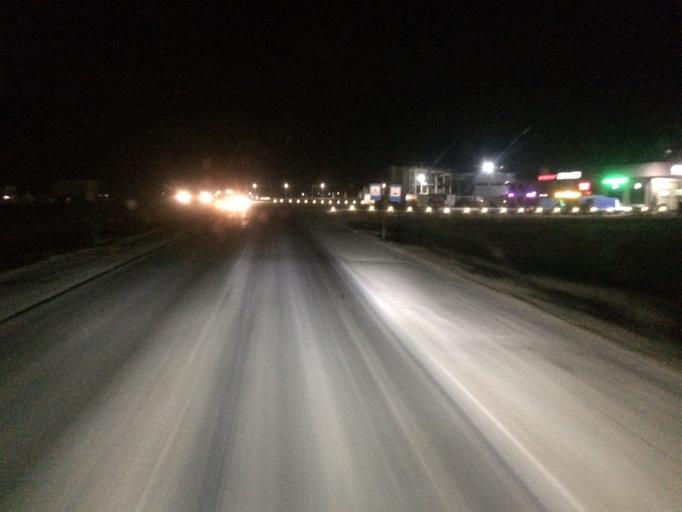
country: KZ
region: Batys Qazaqstan
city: Oral
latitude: 51.2724
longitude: 51.4016
